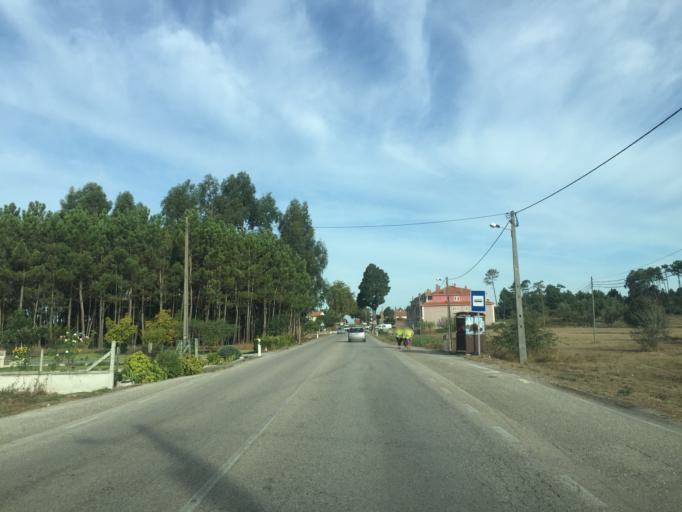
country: PT
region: Leiria
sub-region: Pombal
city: Lourical
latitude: 39.9591
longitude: -8.7871
